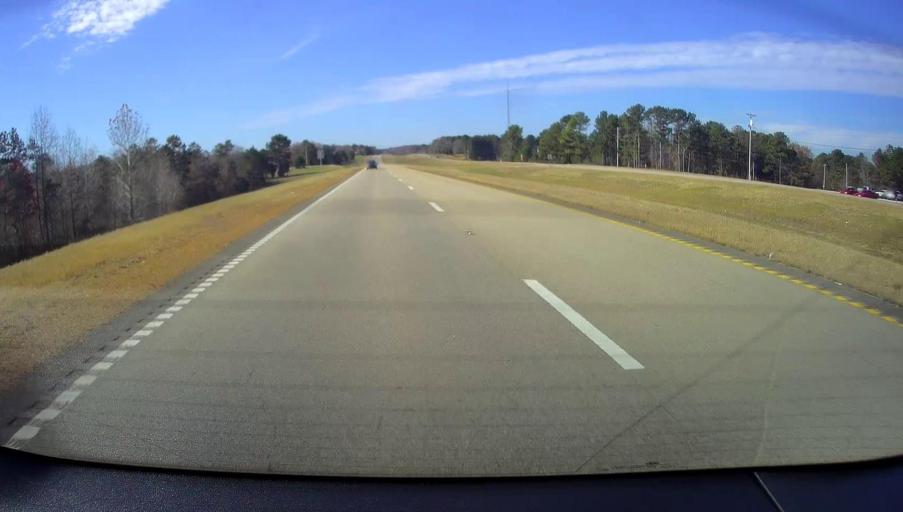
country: US
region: Mississippi
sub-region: Benton County
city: Ashland
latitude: 34.9530
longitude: -89.0085
